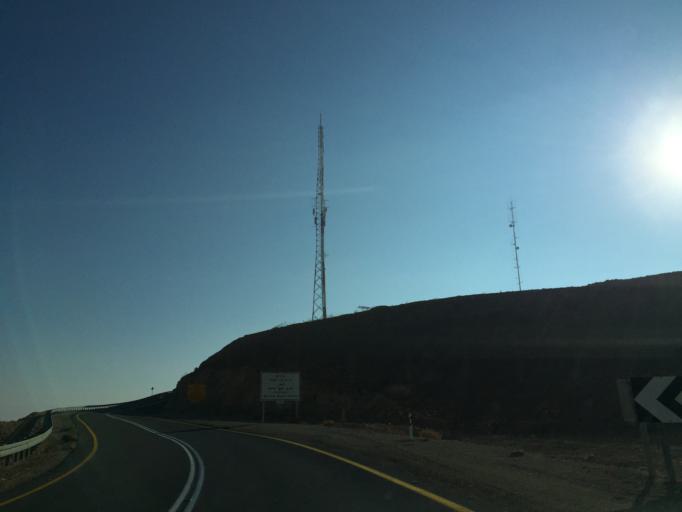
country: JO
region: Ma'an
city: Al Quwayrah
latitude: 30.0211
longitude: 35.0580
